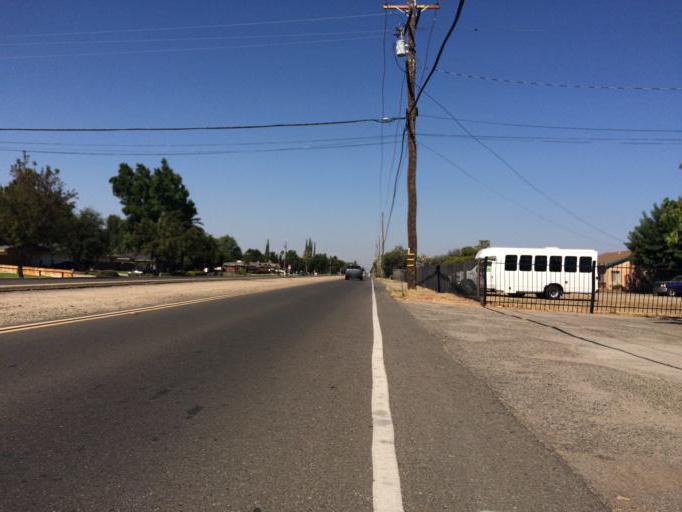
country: US
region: California
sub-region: Fresno County
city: Sunnyside
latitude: 36.7504
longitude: -119.6923
